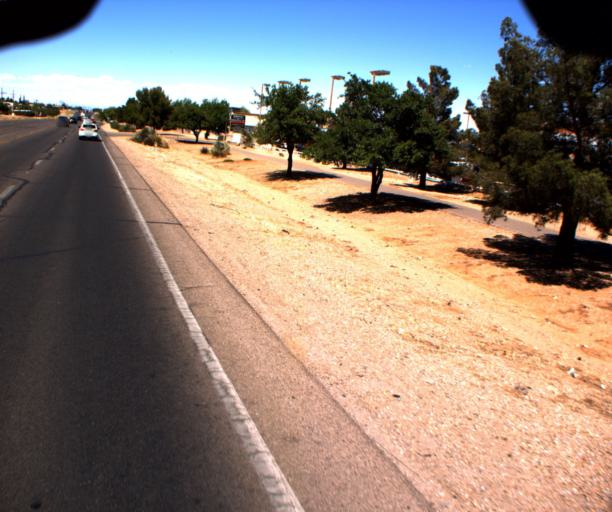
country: US
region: Arizona
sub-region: Cochise County
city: Sierra Vista
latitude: 31.5370
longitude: -110.2573
